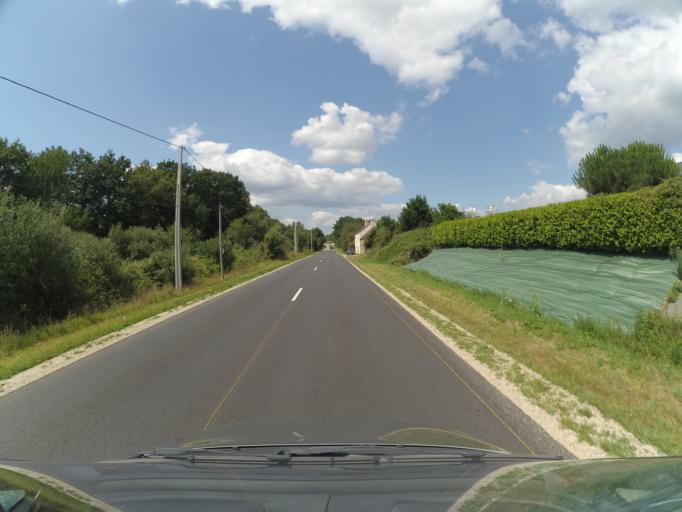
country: FR
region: Brittany
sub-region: Departement du Morbihan
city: Landevant
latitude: 47.7523
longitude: -3.1081
